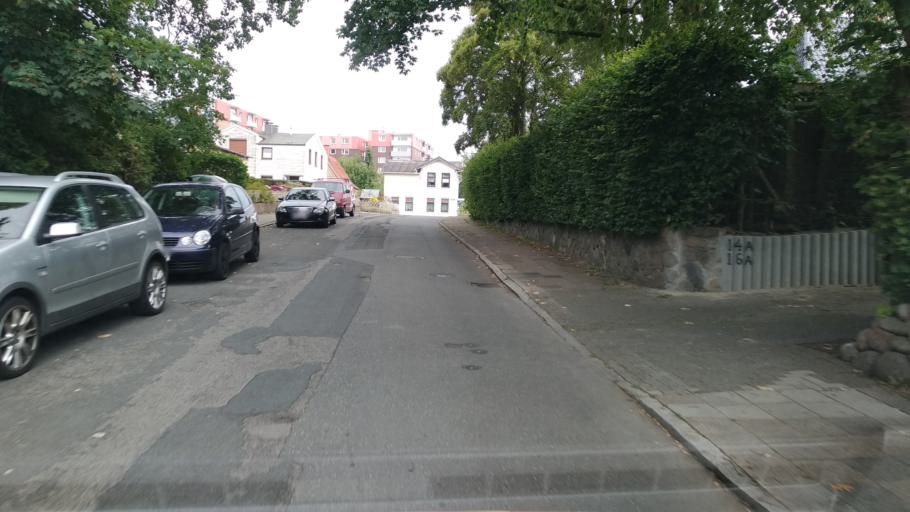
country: DE
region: Schleswig-Holstein
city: Schleswig
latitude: 54.5199
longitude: 9.5754
